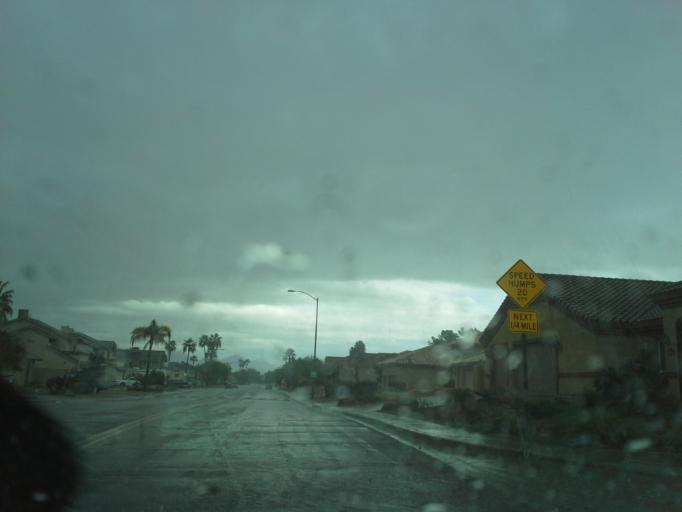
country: US
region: Arizona
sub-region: Maricopa County
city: Paradise Valley
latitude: 33.6331
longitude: -112.0481
